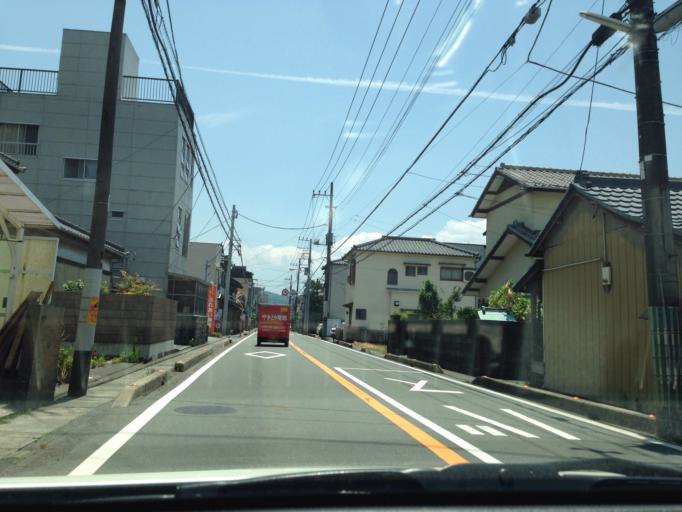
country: JP
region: Shizuoka
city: Numazu
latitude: 35.0541
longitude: 138.8844
